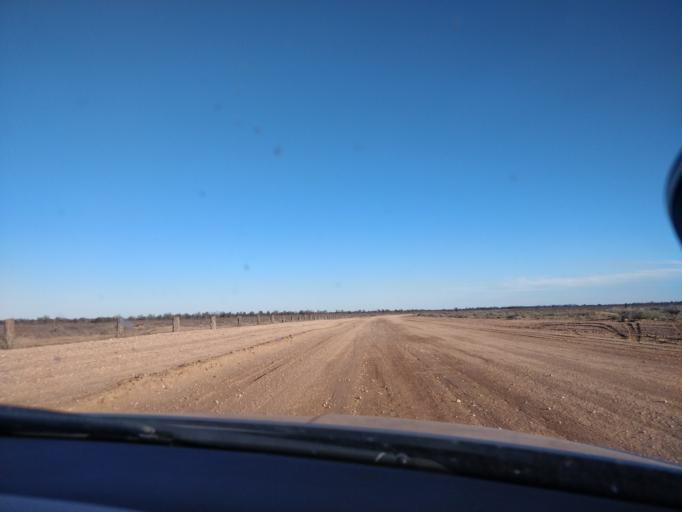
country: AU
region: New South Wales
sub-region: Wentworth
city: Gol Gol
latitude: -33.8332
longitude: 142.8991
